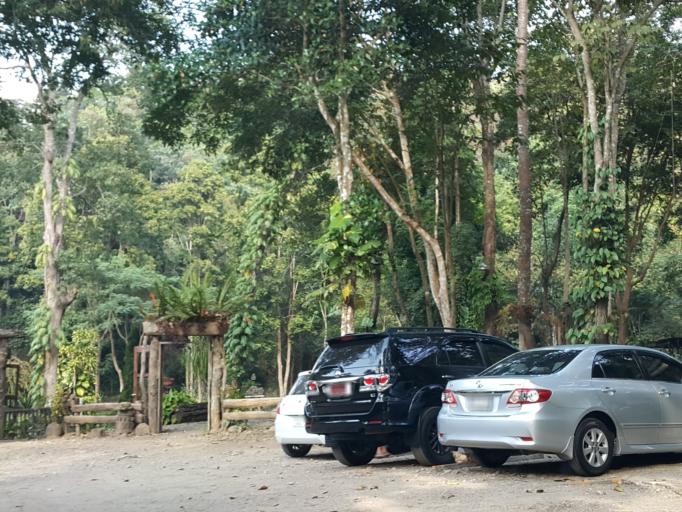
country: TH
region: Chiang Mai
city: Mae On
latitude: 18.8678
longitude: 99.3075
